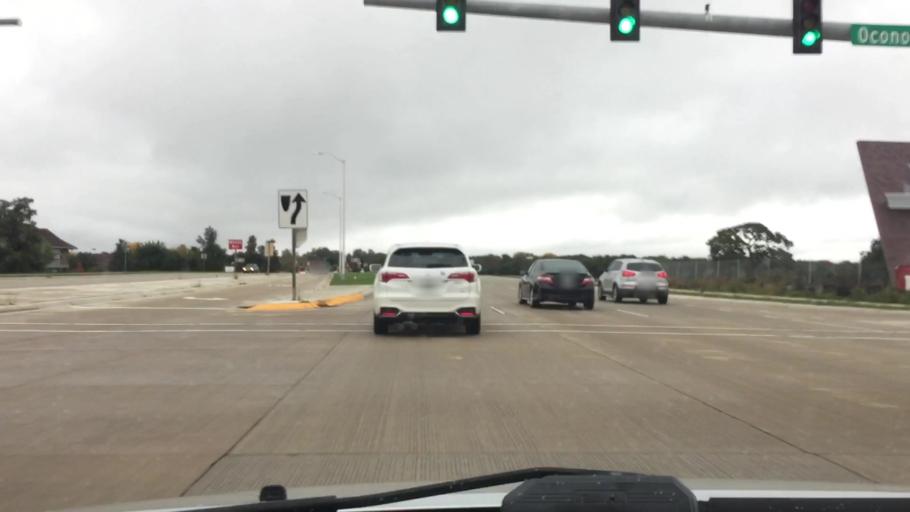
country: US
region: Wisconsin
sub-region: Waukesha County
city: Oconomowoc
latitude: 43.0816
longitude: -88.4705
